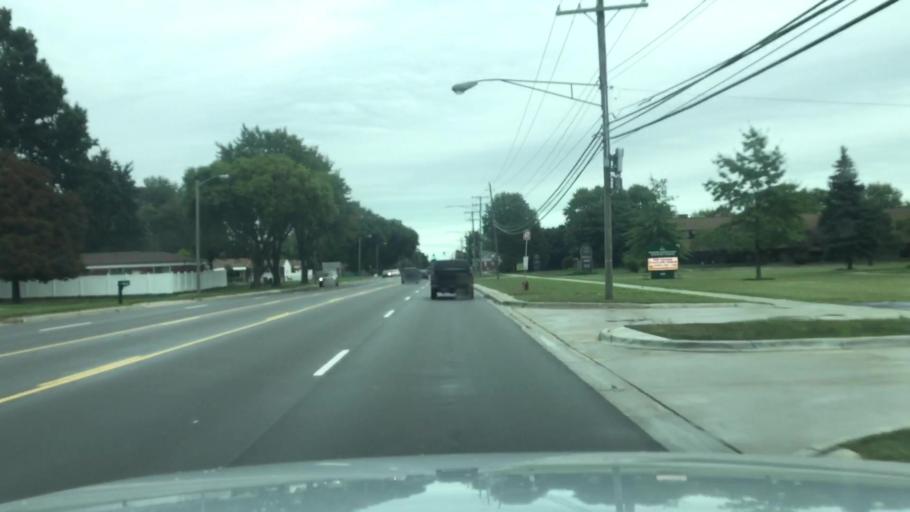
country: US
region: Michigan
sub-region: Macomb County
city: Center Line
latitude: 42.5214
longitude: -83.0038
